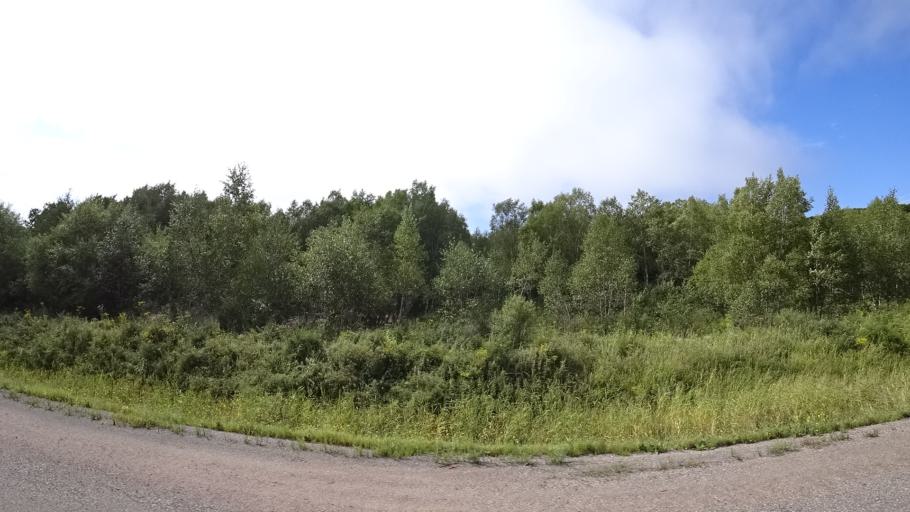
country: RU
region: Primorskiy
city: Lyalichi
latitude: 44.1169
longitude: 132.4191
